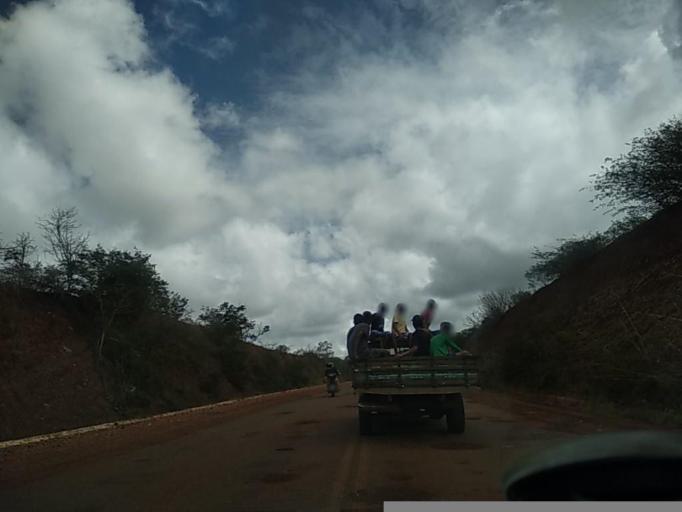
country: BR
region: Bahia
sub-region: Caetite
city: Caetite
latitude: -14.0267
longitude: -42.4885
